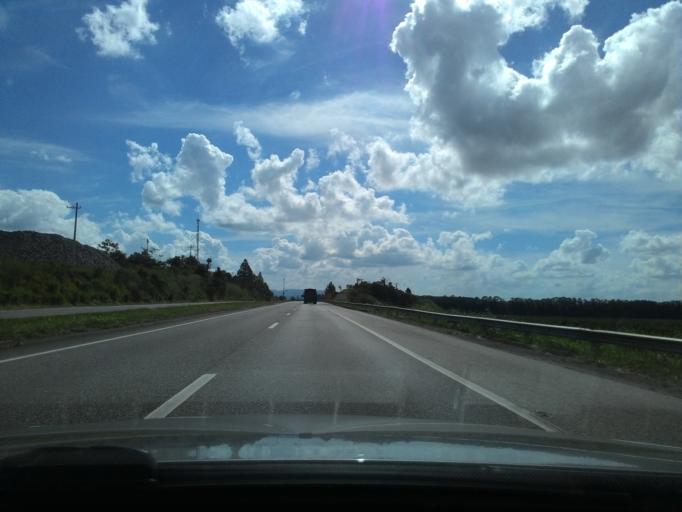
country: BR
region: Sao Paulo
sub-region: Cajati
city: Cajati
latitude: -24.7221
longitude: -48.0623
